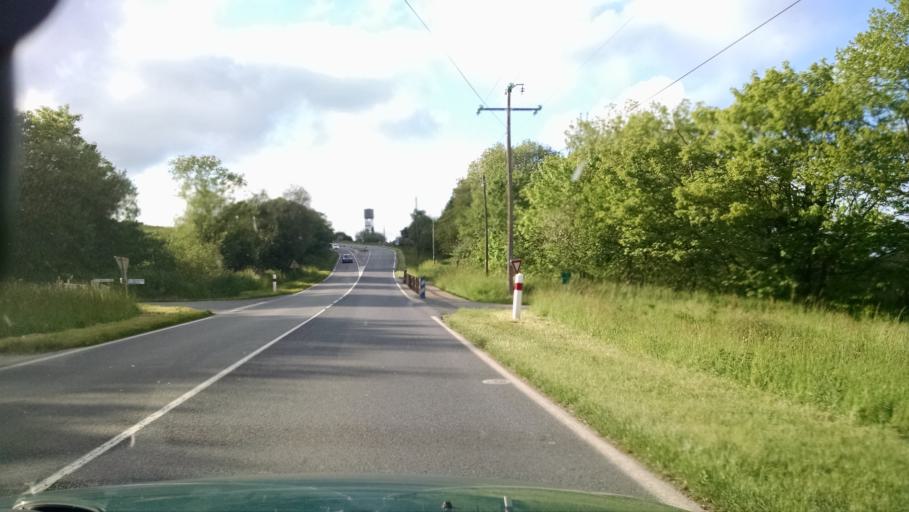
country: FR
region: Brittany
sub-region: Departement du Finistere
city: Henvic
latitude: 48.6474
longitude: -3.9575
